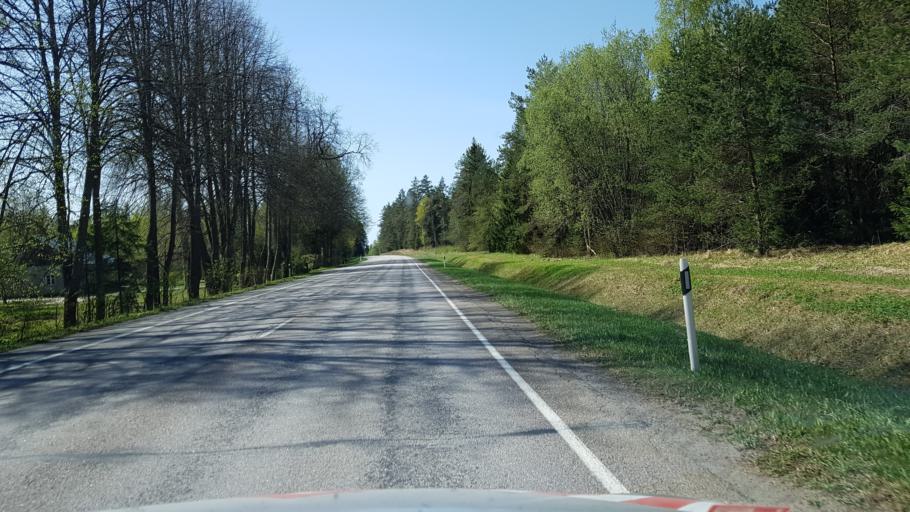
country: EE
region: Valgamaa
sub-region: Valga linn
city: Valga
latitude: 57.8175
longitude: 26.0456
